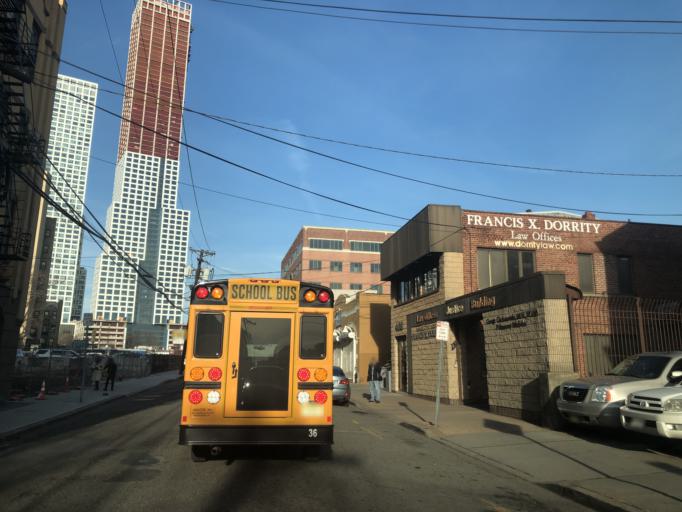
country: US
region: New Jersey
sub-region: Hudson County
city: Jersey City
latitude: 40.7293
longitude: -74.0621
